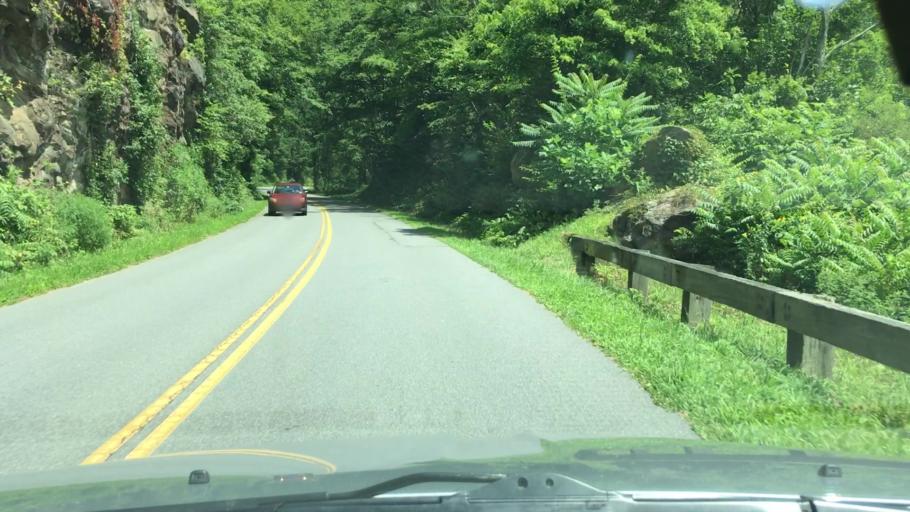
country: US
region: North Carolina
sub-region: Buncombe County
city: Swannanoa
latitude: 35.6665
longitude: -82.4682
